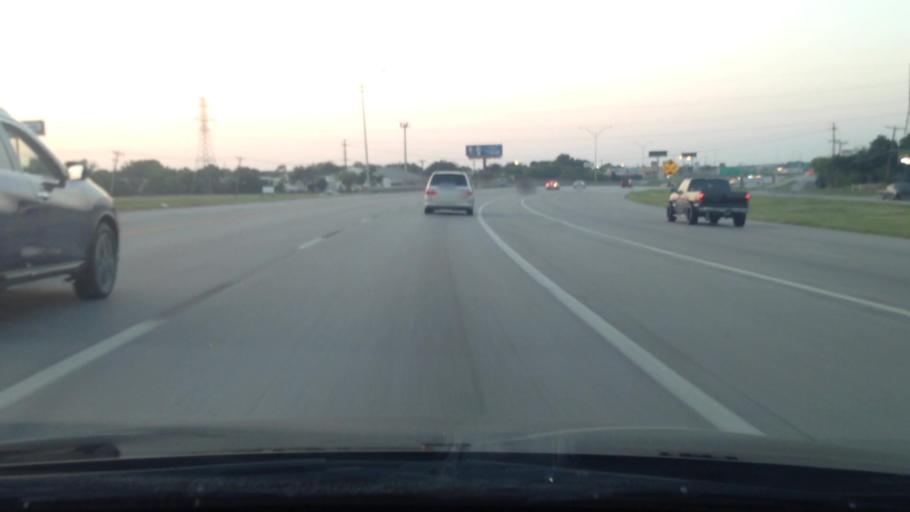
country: US
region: Texas
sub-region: Tarrant County
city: Forest Hill
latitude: 32.6724
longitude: -97.2400
